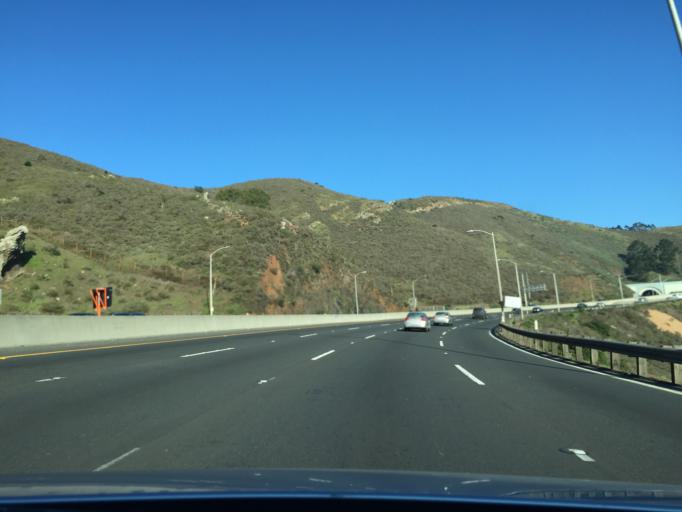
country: US
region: California
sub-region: Marin County
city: Sausalito
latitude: 37.8387
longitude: -122.4866
